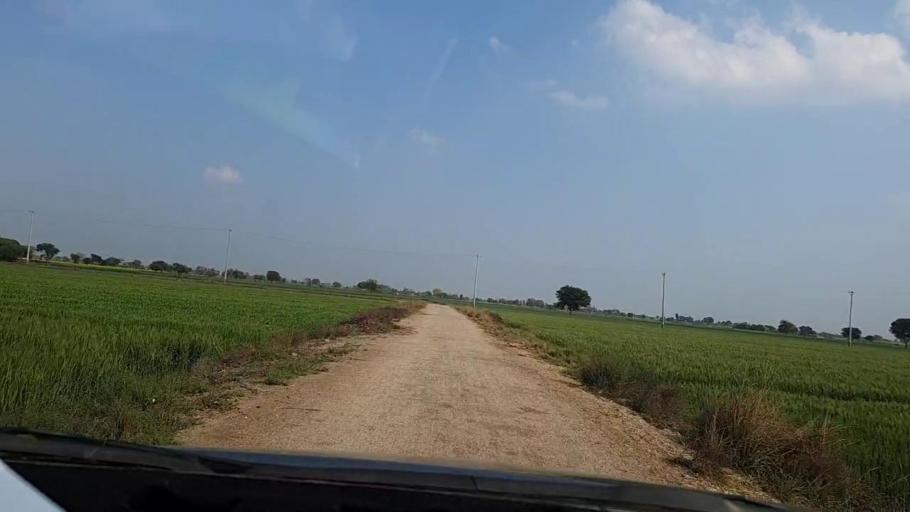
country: PK
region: Sindh
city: Nawabshah
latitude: 26.1675
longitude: 68.3629
